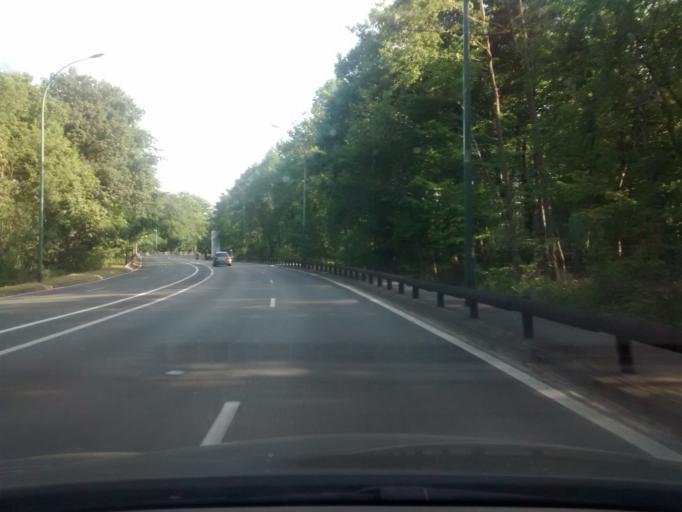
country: FR
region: Ile-de-France
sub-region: Departement des Hauts-de-Seine
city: Vaucresson
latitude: 48.8216
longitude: 2.1515
